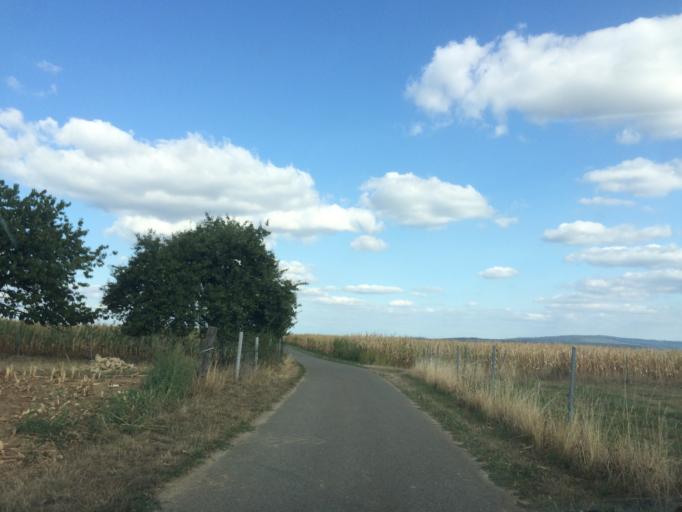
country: DE
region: Hesse
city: Trendelburg
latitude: 51.6115
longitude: 9.3837
